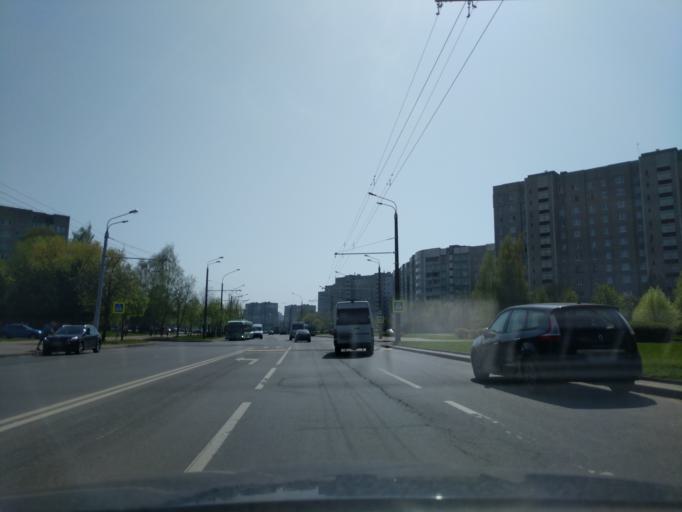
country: BY
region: Minsk
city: Malinovka
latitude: 53.8632
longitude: 27.4563
